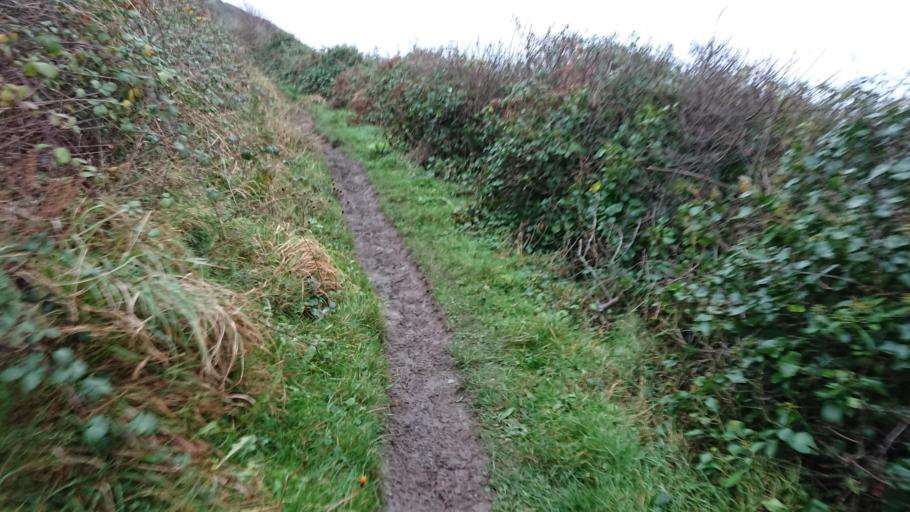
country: GB
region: England
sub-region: Cornwall
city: Fowey
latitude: 50.3325
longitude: -4.5772
